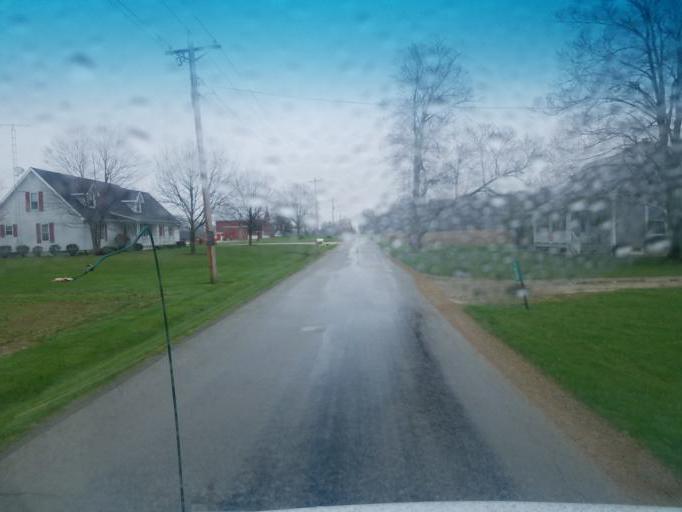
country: US
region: Ohio
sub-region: Seneca County
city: Tiffin
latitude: 40.9643
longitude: -83.1452
